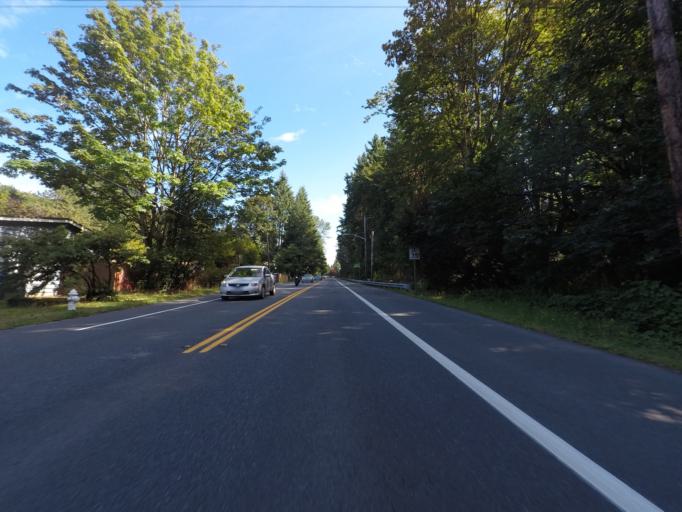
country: US
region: Washington
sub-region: King County
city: Kenmore
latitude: 47.7356
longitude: -122.2482
